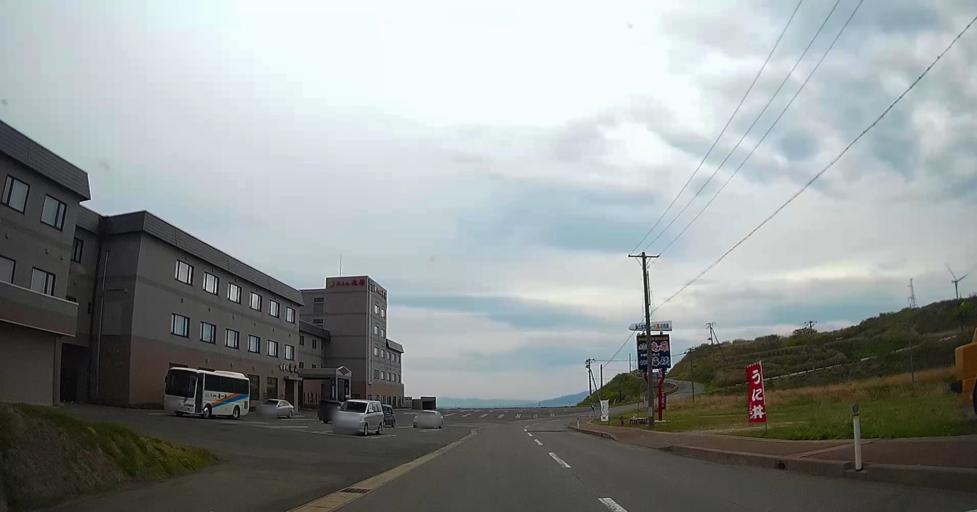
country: JP
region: Aomori
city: Shimokizukuri
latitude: 41.2570
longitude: 140.3470
